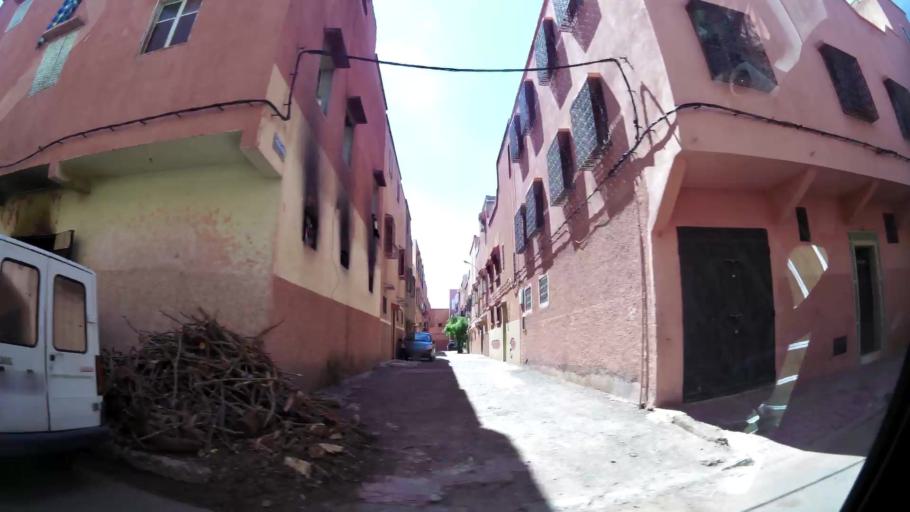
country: MA
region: Marrakech-Tensift-Al Haouz
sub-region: Marrakech
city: Marrakesh
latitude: 31.6027
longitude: -7.9700
